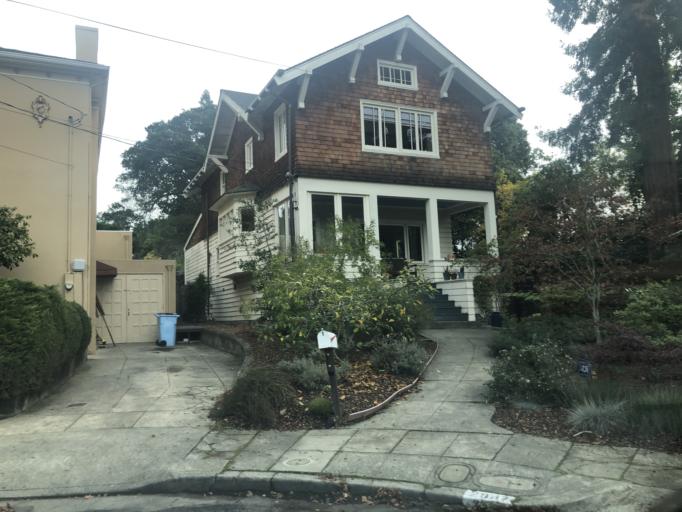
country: US
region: California
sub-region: Alameda County
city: Berkeley
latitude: 37.8572
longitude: -122.2475
